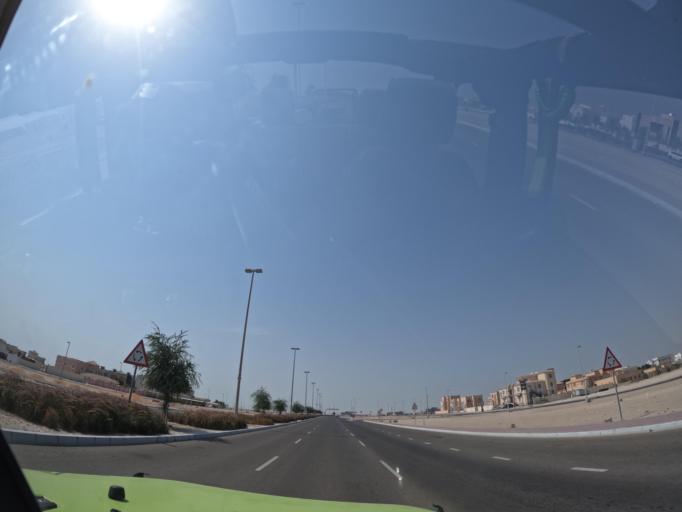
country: AE
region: Abu Dhabi
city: Abu Dhabi
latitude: 24.3554
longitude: 54.6153
